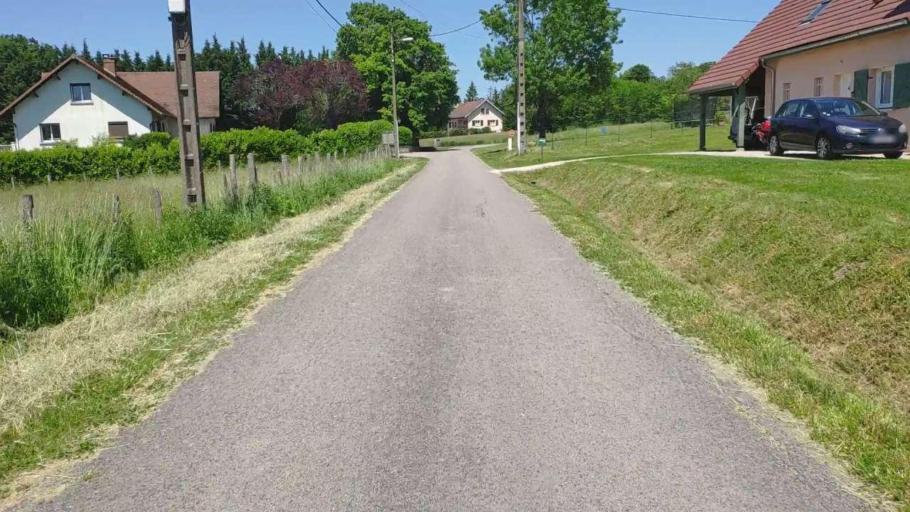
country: FR
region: Franche-Comte
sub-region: Departement du Jura
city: Bletterans
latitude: 46.7433
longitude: 5.4104
